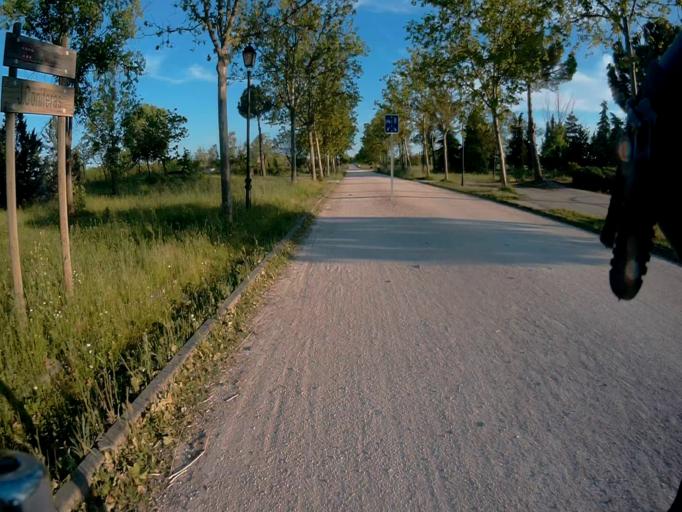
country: ES
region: Madrid
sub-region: Provincia de Madrid
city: Alcorcon
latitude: 40.3237
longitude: -3.8004
